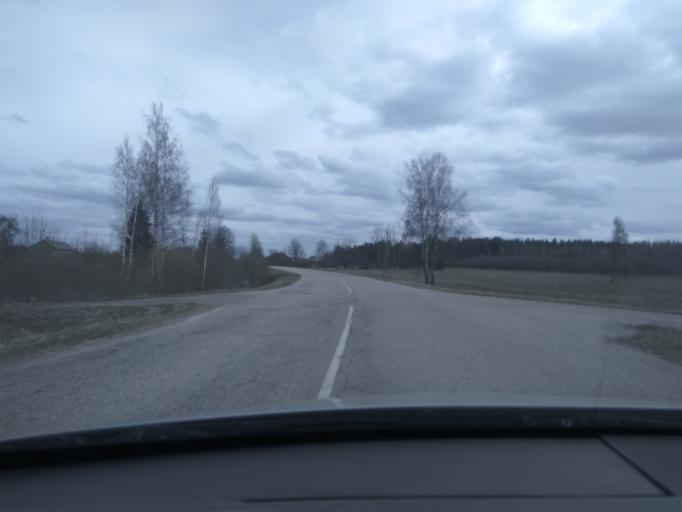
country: LV
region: Aizpute
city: Aizpute
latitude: 56.7759
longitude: 21.5206
